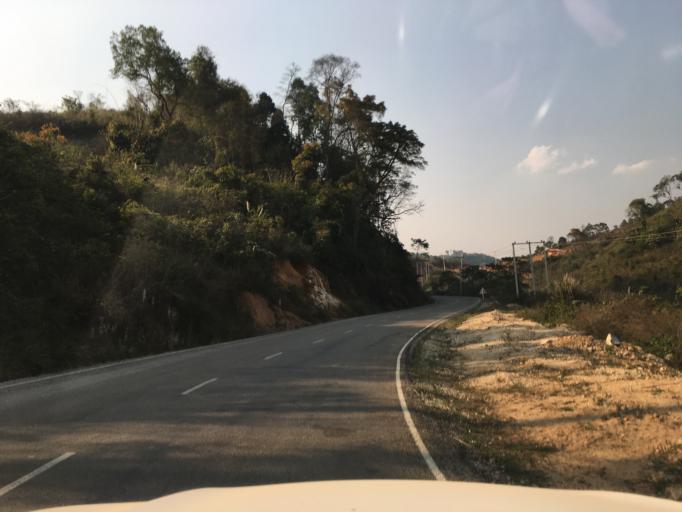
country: LA
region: Houaphan
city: Xam Nua
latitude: 20.5711
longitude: 104.0578
